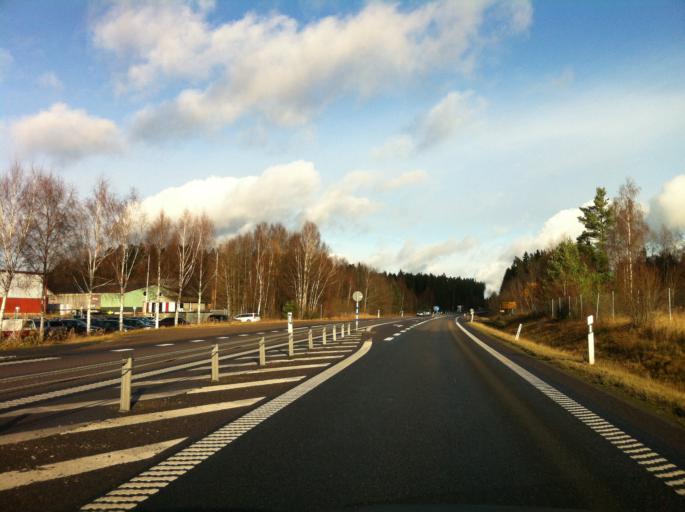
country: SE
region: Skane
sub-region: Osby Kommun
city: Osby
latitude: 56.4026
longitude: 14.0396
